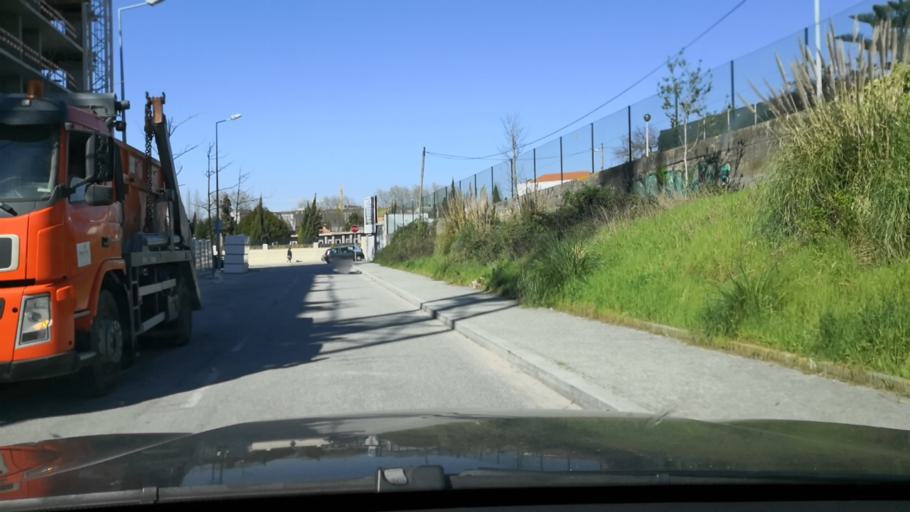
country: PT
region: Porto
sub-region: Porto
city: Porto
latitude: 41.1731
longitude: -8.6012
